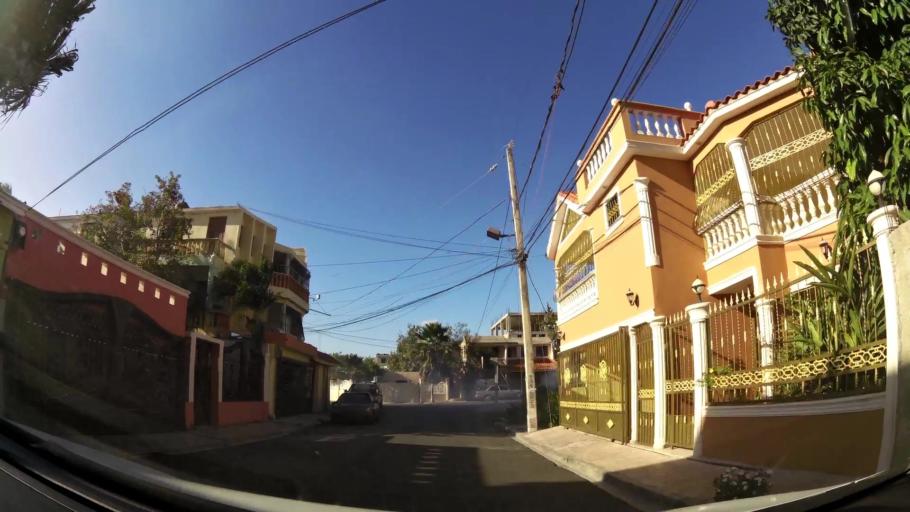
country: DO
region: Santo Domingo
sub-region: Santo Domingo
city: Santo Domingo Este
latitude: 18.4875
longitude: -69.8066
